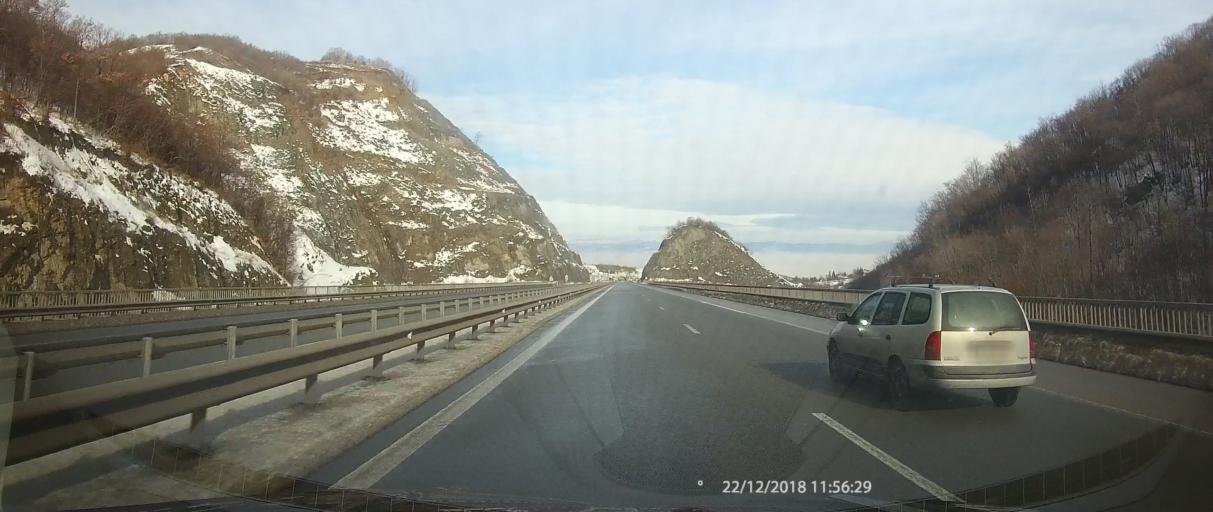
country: BG
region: Sofiya
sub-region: Obshtina Bozhurishte
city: Bozhurishte
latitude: 42.6696
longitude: 23.1503
